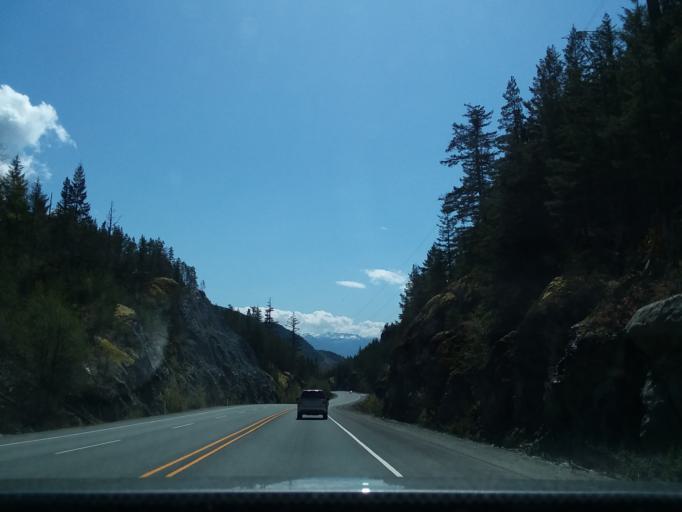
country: CA
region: British Columbia
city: Whistler
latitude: 49.9013
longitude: -123.1630
